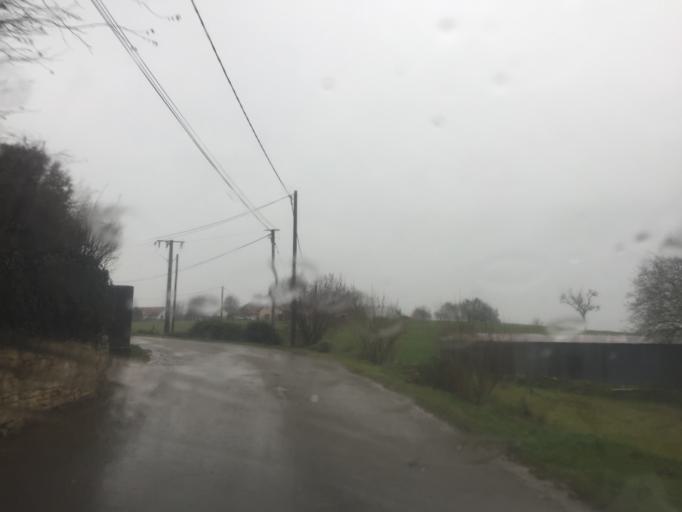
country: FR
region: Franche-Comte
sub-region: Departement du Jura
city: Dampierre
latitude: 47.2244
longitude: 5.7074
